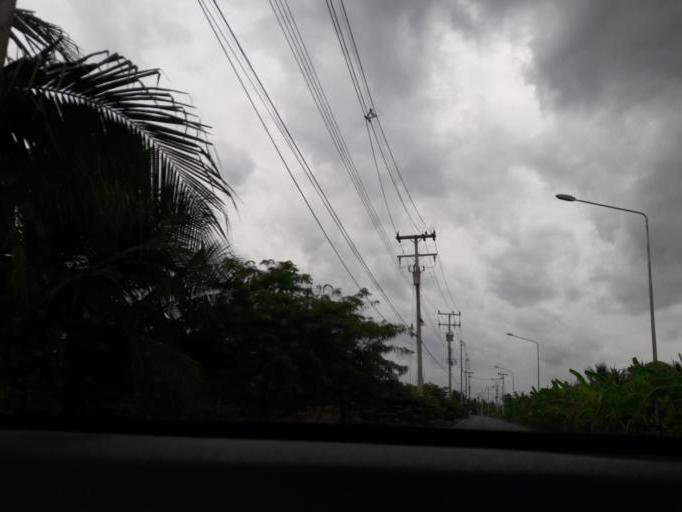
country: TH
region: Ratchaburi
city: Damnoen Saduak
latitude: 13.5729
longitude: 99.9833
